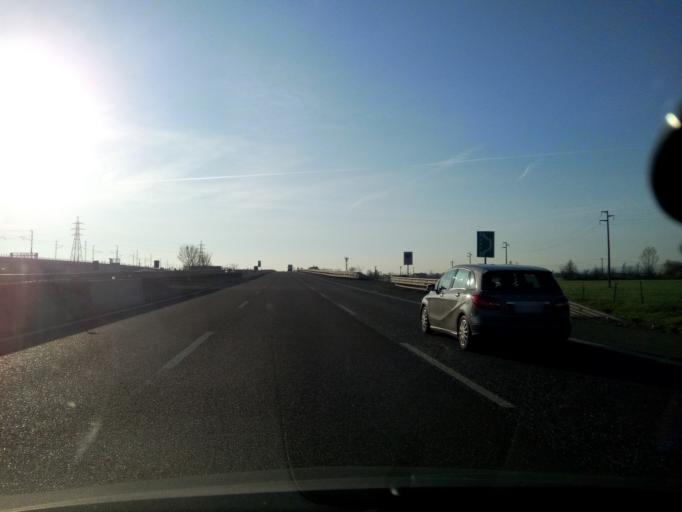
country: IT
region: Emilia-Romagna
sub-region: Provincia di Parma
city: Fidenza
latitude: 44.9012
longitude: 10.0381
